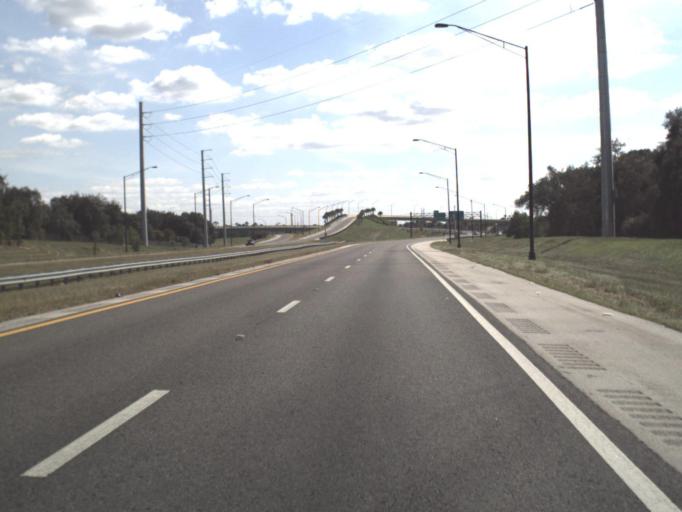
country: US
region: Florida
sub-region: Polk County
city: Loughman
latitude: 28.2886
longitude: -81.5977
